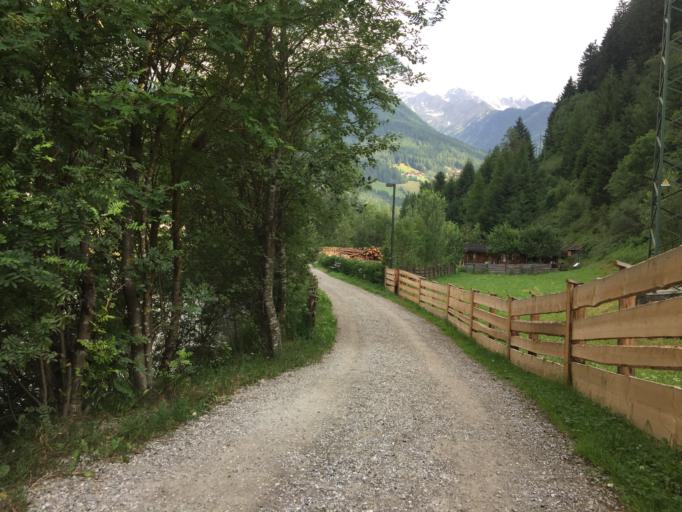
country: IT
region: Trentino-Alto Adige
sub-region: Bolzano
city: Molini di Tures
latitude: 46.9489
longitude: 11.9237
